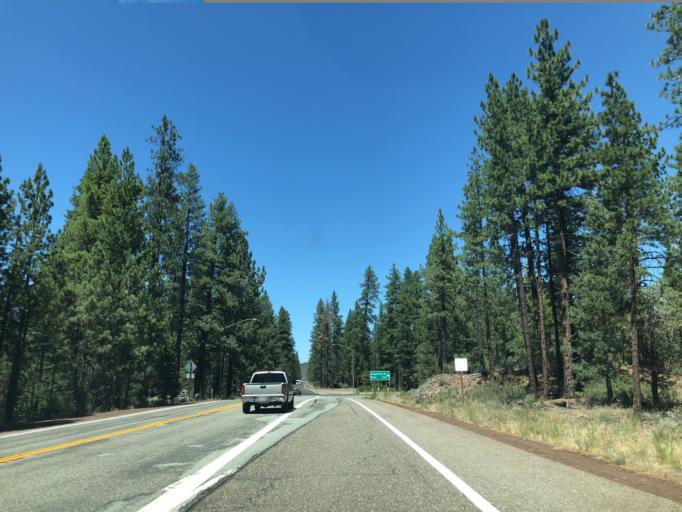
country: US
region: California
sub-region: Shasta County
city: Burney
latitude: 40.6796
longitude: -121.4251
